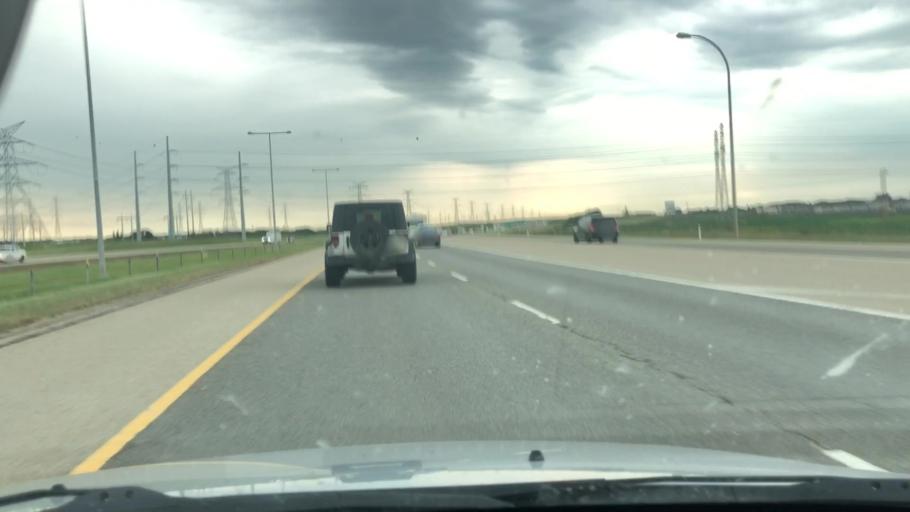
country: CA
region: Alberta
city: Beaumont
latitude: 53.4367
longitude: -113.3769
